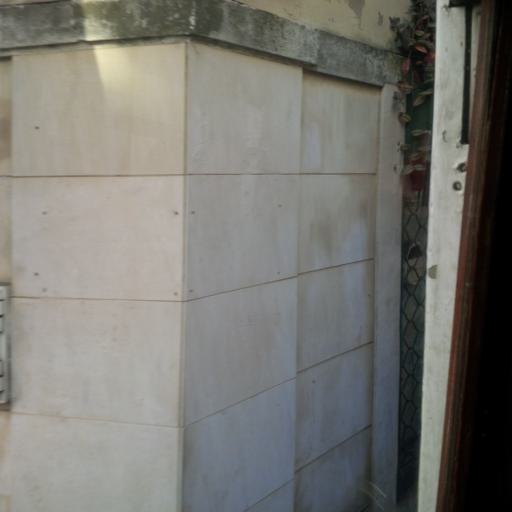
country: PT
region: Lisbon
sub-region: Lisbon
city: Lisbon
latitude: 38.7106
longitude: -9.1515
